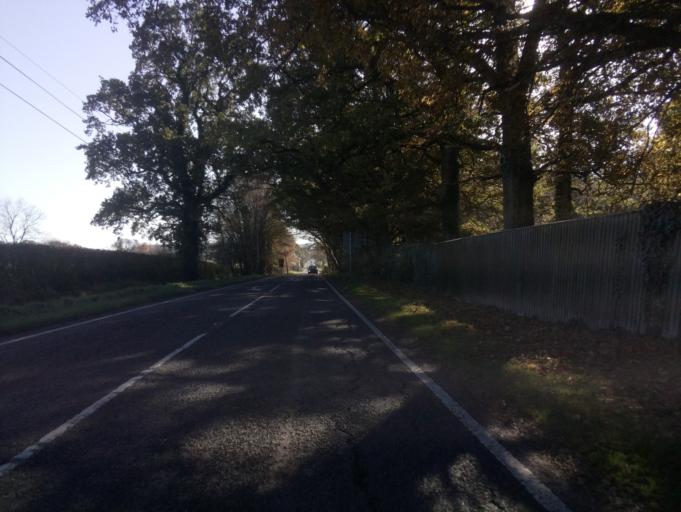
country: GB
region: England
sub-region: Dorset
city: Sherborne
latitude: 50.8781
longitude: -2.4835
